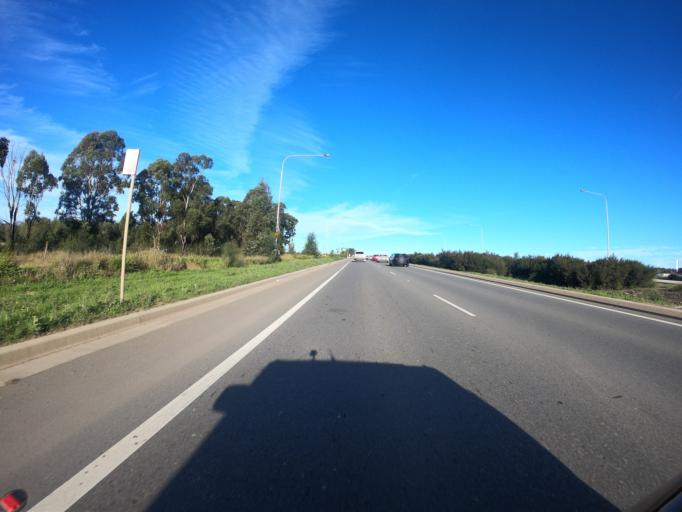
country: AU
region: New South Wales
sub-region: Blacktown
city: Riverstone
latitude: -33.6943
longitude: 150.8289
